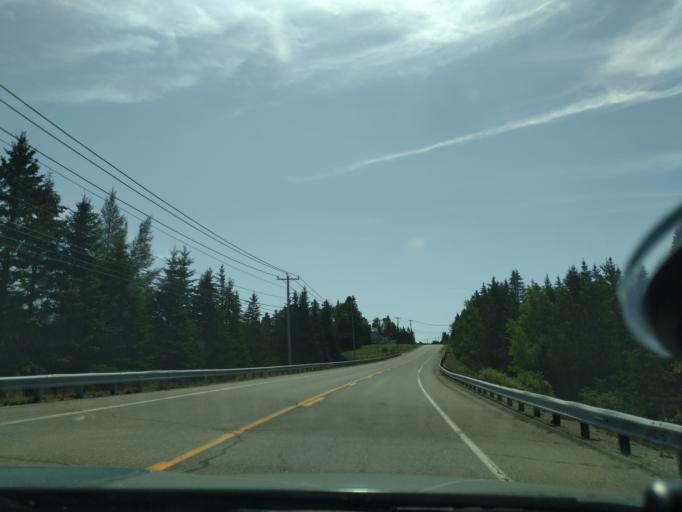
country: US
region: Maine
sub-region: Washington County
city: Addison
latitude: 44.6535
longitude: -67.7167
